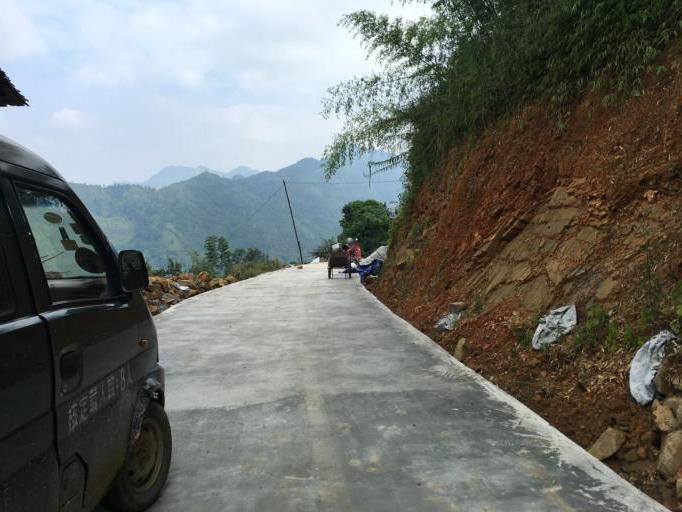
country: CN
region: Guangxi Zhuangzu Zizhiqu
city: Tongle
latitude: 25.2973
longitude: 106.1636
